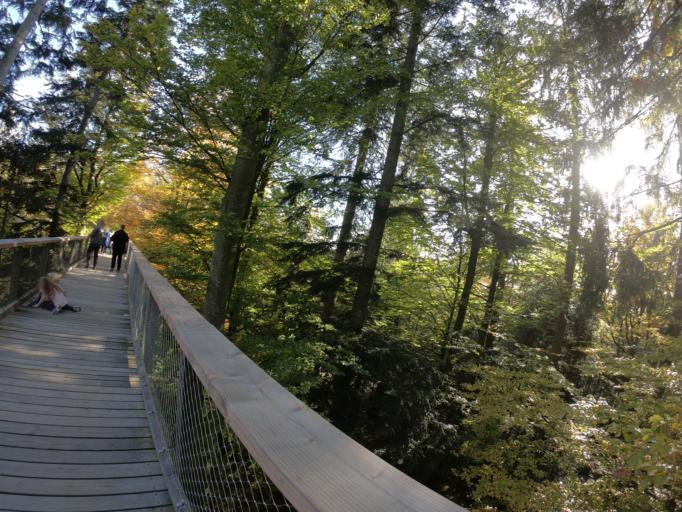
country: DE
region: Bavaria
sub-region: Lower Bavaria
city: Neuschonau
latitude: 48.8907
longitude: 13.4847
